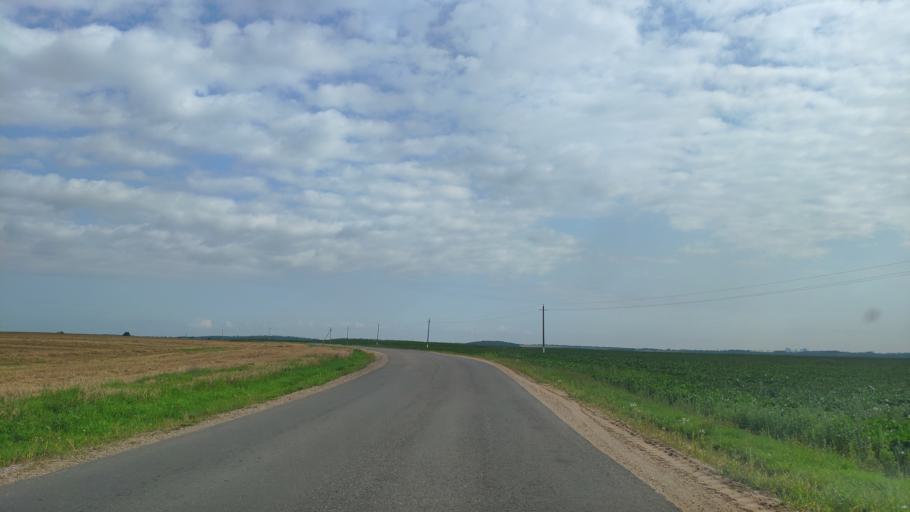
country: BY
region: Minsk
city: Khatsyezhyna
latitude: 53.8418
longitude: 27.3128
